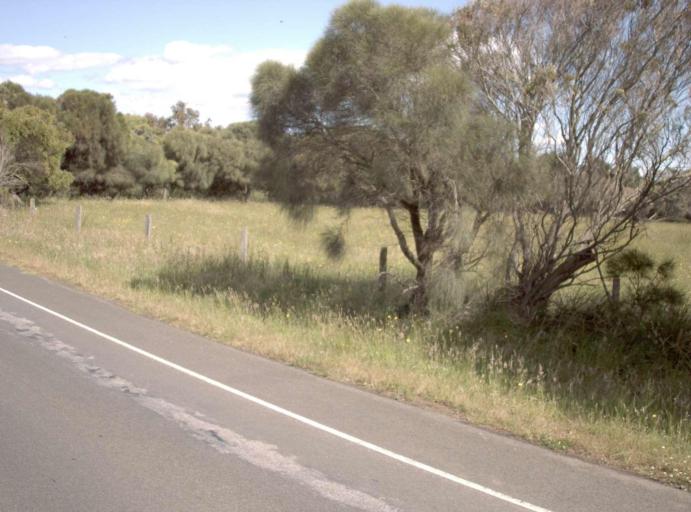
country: AU
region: Victoria
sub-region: Bass Coast
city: Phillip Island
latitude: -38.4967
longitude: 145.2209
